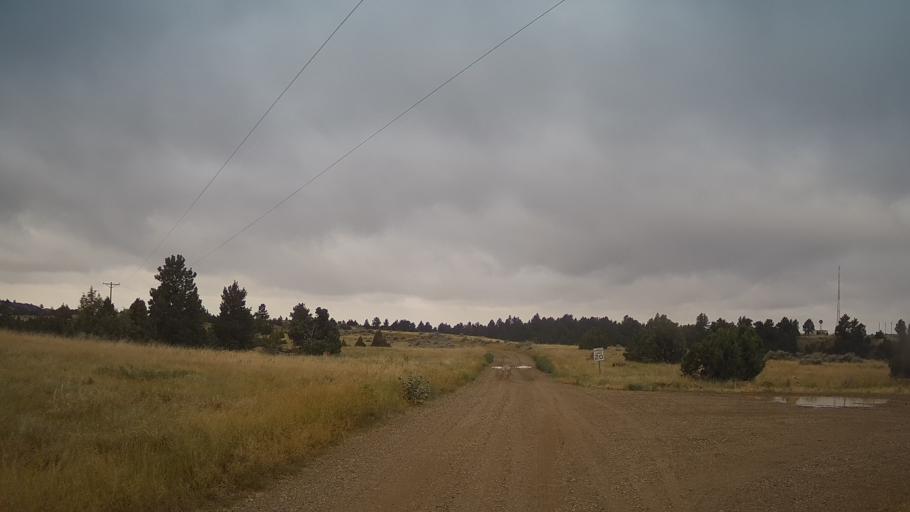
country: US
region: Montana
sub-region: Dawson County
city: Glendive
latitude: 47.0480
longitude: -104.6783
